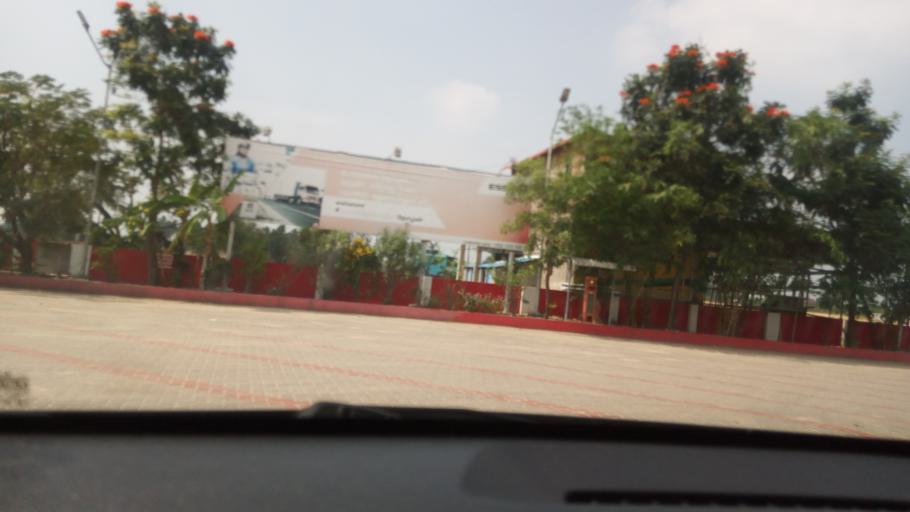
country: IN
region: Tamil Nadu
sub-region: Kancheepuram
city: Kanchipuram
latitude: 12.8735
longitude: 79.6291
